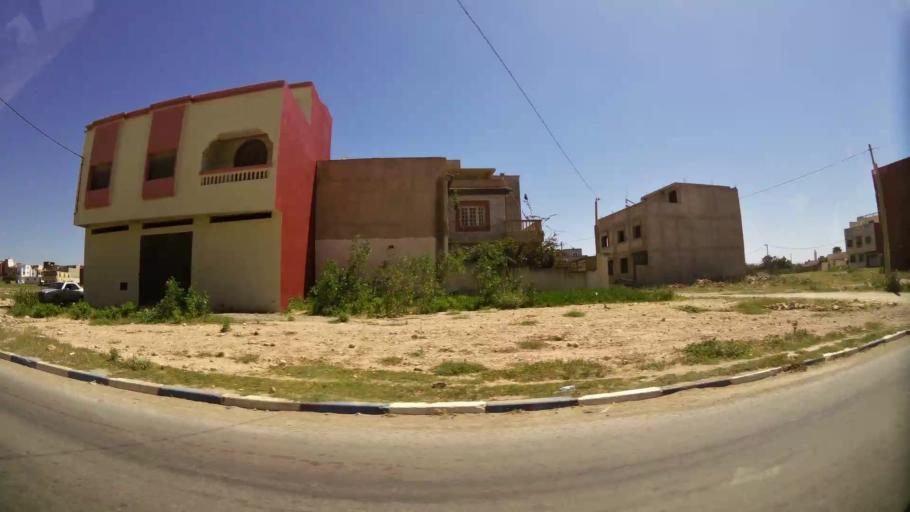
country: MA
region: Oriental
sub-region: Berkane-Taourirt
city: Madagh
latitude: 35.1355
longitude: -2.4106
